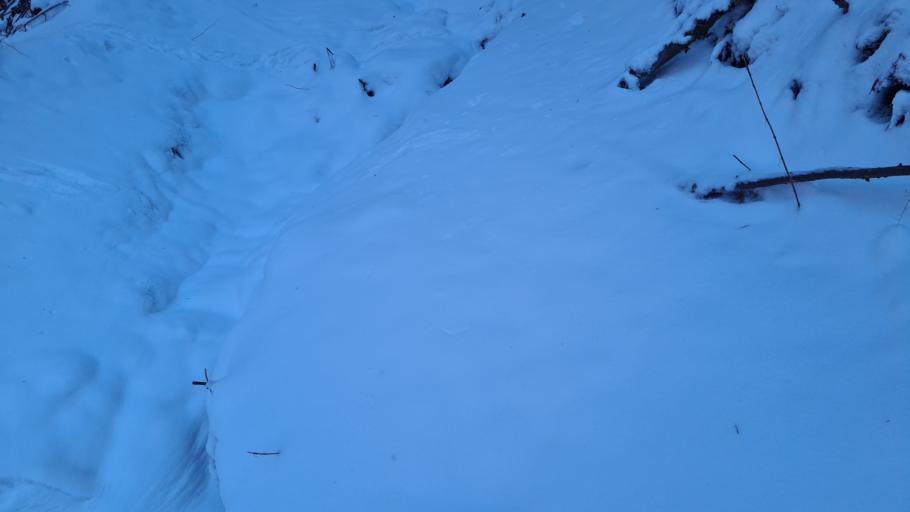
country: HR
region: Varazdinska
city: Ivanec
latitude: 46.1793
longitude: 16.0991
